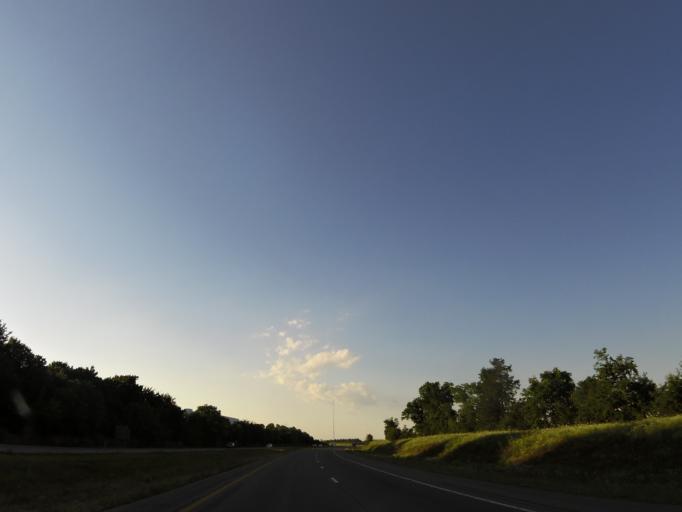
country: US
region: Tennessee
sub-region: Wilson County
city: Rural Hill
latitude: 36.0577
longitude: -86.4317
